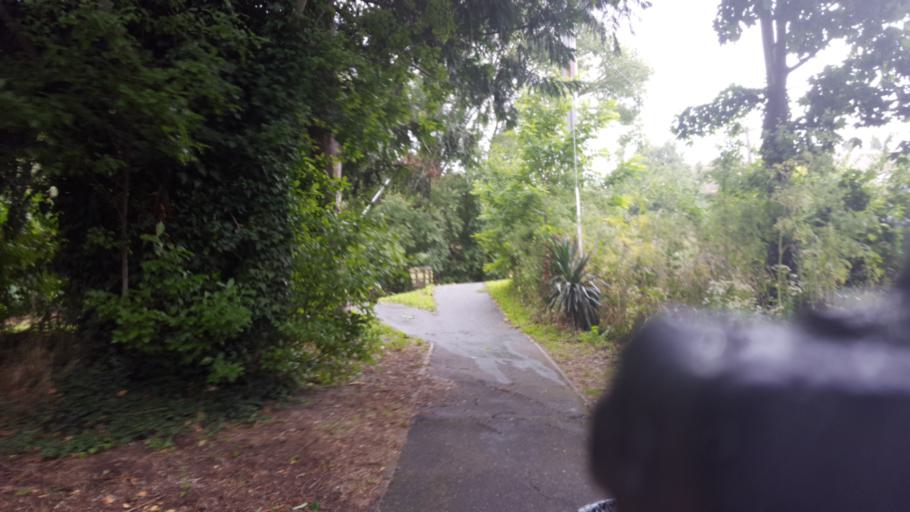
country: NZ
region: Otago
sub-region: Queenstown-Lakes District
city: Wanaka
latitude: -45.1846
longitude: 169.3157
